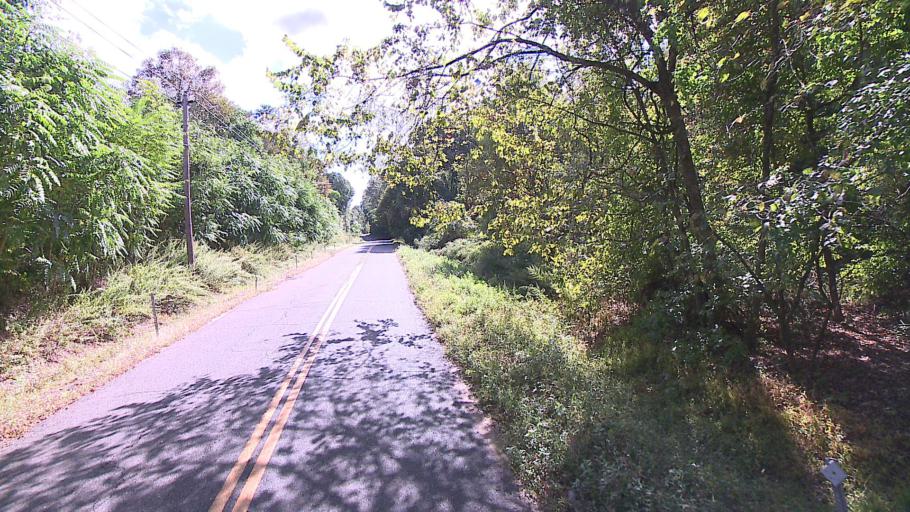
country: US
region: Connecticut
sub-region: Fairfield County
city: Shelton
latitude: 41.3475
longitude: -73.1304
